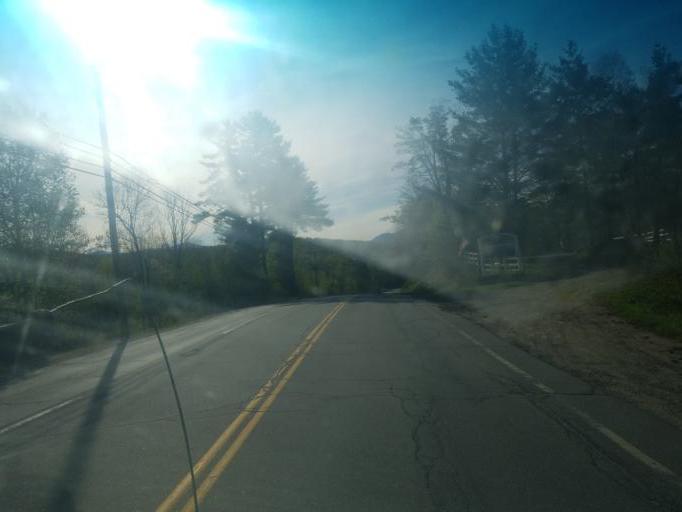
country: US
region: New Hampshire
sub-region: Grafton County
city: Deerfield
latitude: 44.2778
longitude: -71.6437
